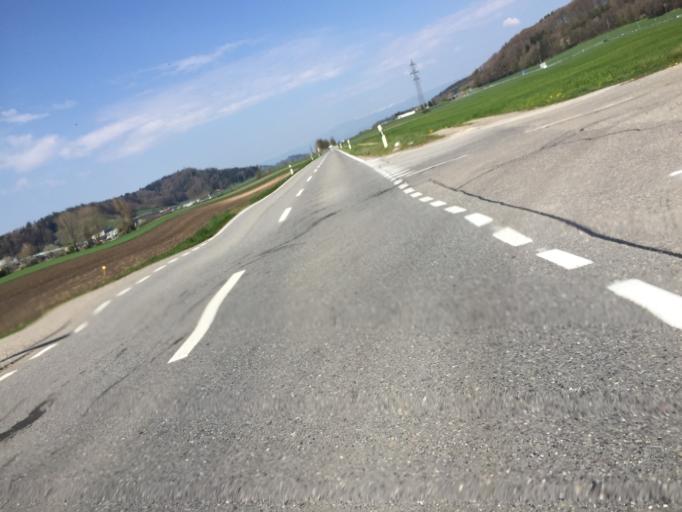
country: CH
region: Bern
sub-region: Bern-Mittelland District
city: Munchenbuchsee
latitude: 47.0309
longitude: 7.4522
